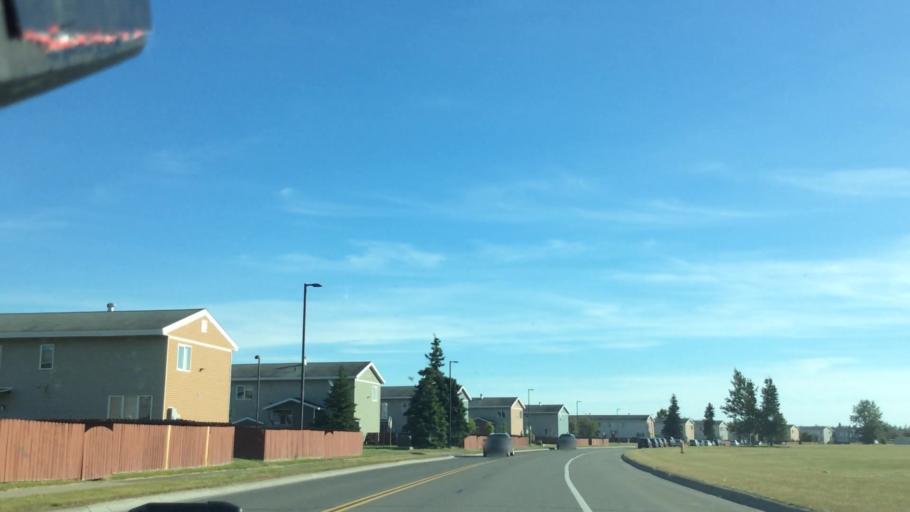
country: US
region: Alaska
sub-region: Anchorage Municipality
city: Elmendorf Air Force Base
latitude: 61.2571
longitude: -149.6769
